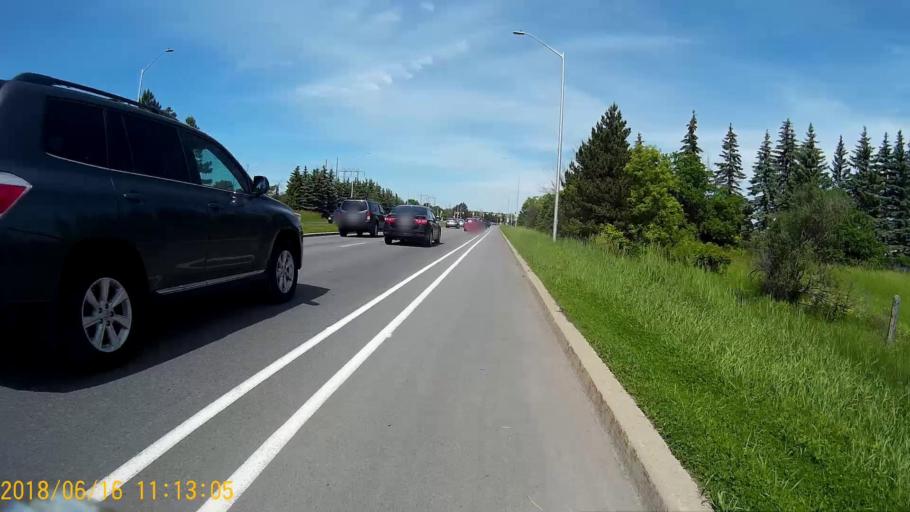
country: CA
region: Ontario
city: Bells Corners
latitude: 45.3340
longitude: -75.9019
